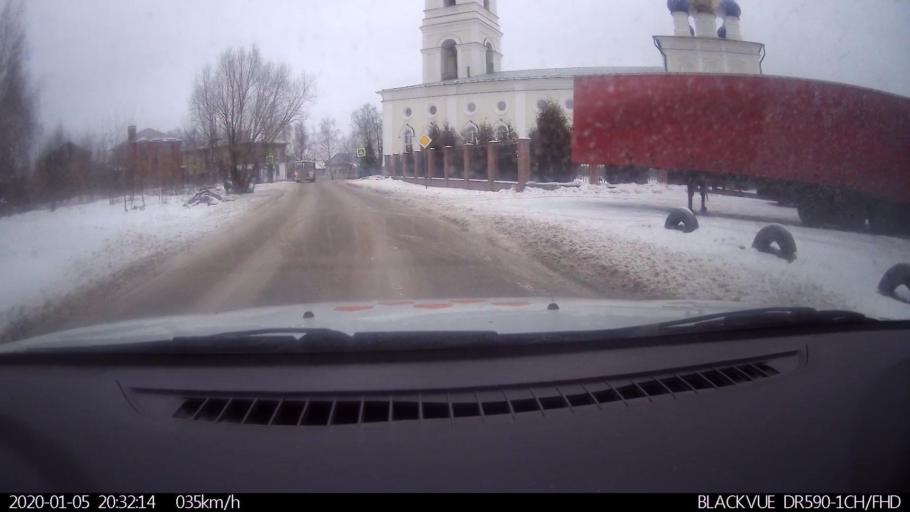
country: RU
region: Nizjnij Novgorod
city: Lukino
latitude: 56.4113
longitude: 43.7294
